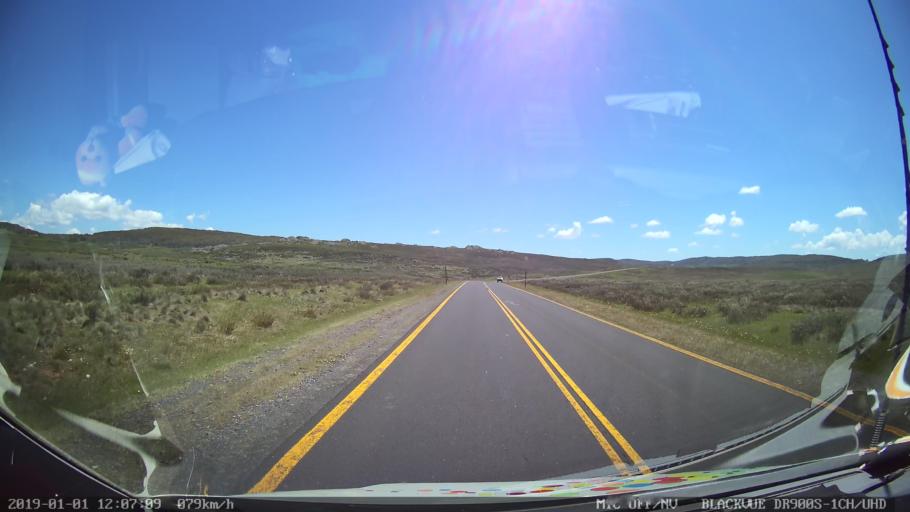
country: AU
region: New South Wales
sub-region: Snowy River
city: Jindabyne
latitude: -35.8365
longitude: 148.4901
